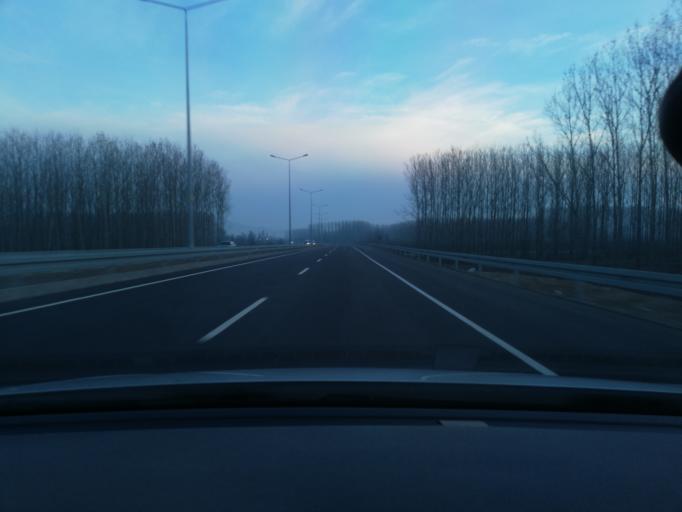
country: TR
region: Duzce
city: Duzce
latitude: 40.8081
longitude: 31.1689
